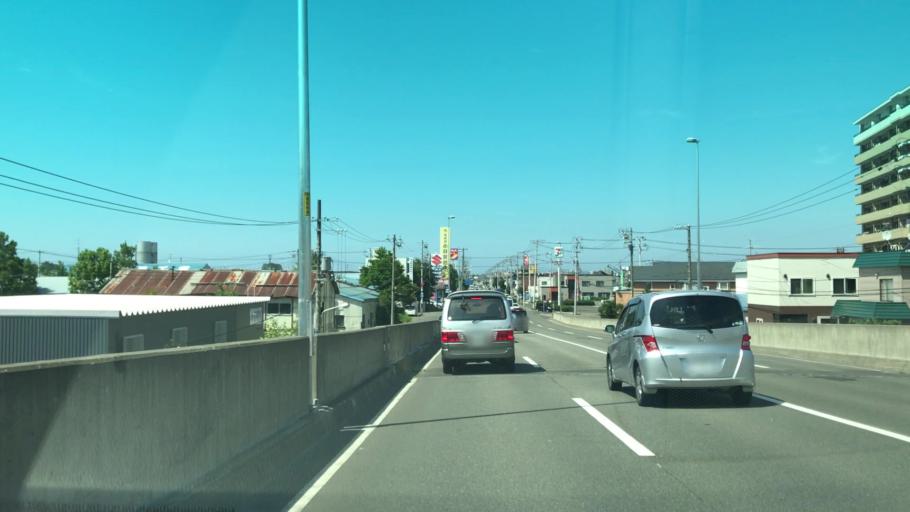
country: JP
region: Hokkaido
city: Sapporo
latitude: 43.1262
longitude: 141.2358
